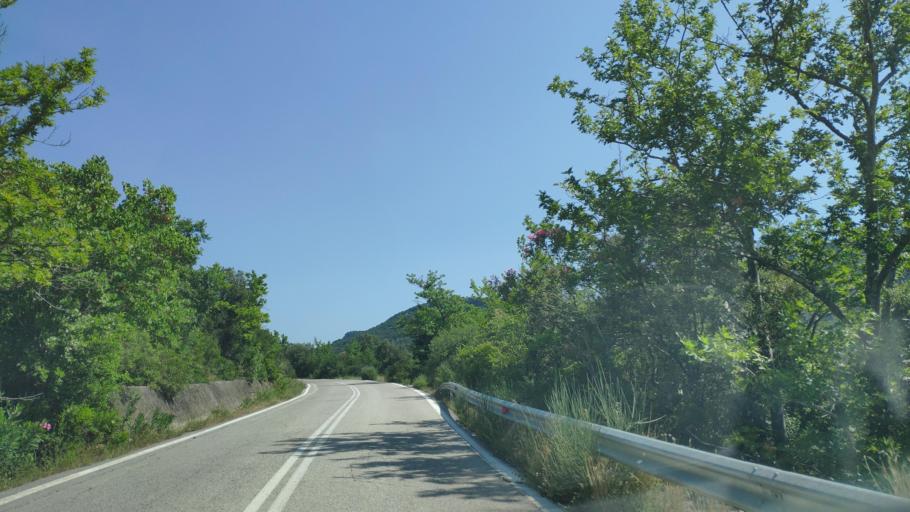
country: GR
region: West Greece
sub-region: Nomos Aitolias kai Akarnanias
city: Lepenou
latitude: 38.7735
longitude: 21.3357
